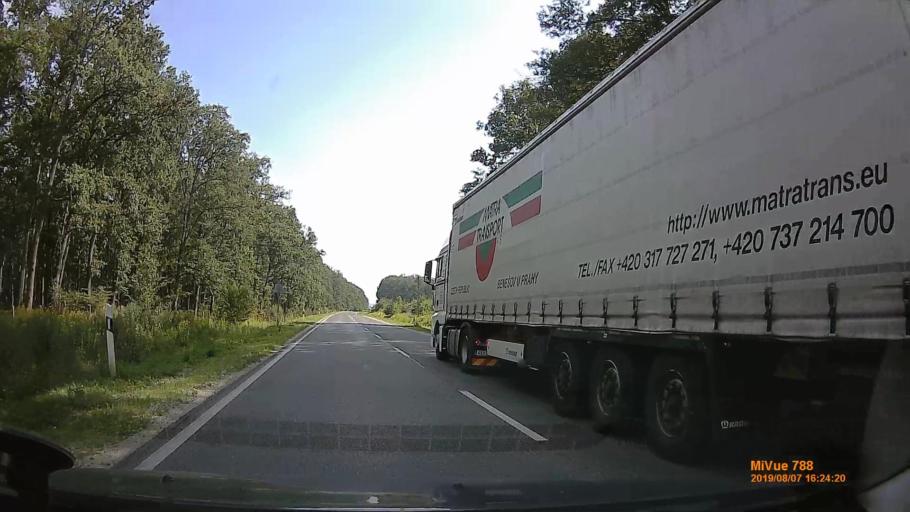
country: HU
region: Zala
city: Lenti
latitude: 46.7374
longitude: 16.5534
